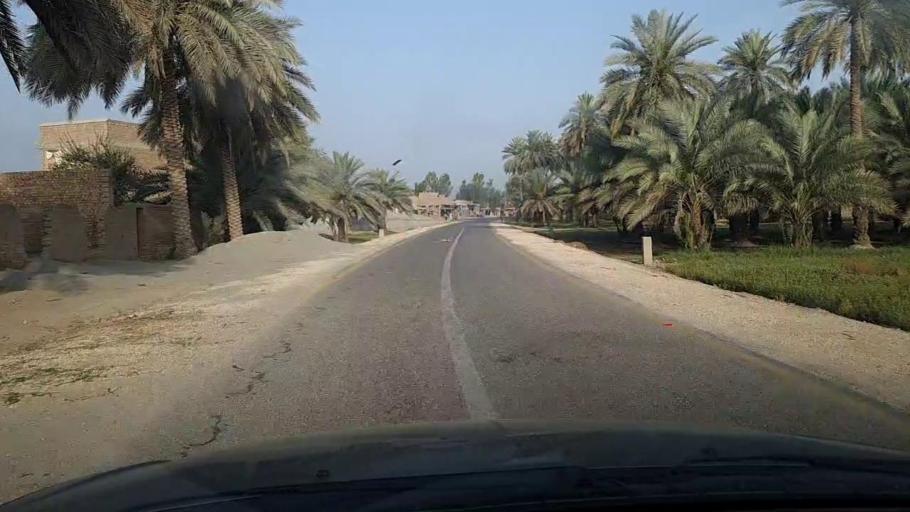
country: PK
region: Sindh
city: Khairpur
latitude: 27.5382
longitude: 68.7132
